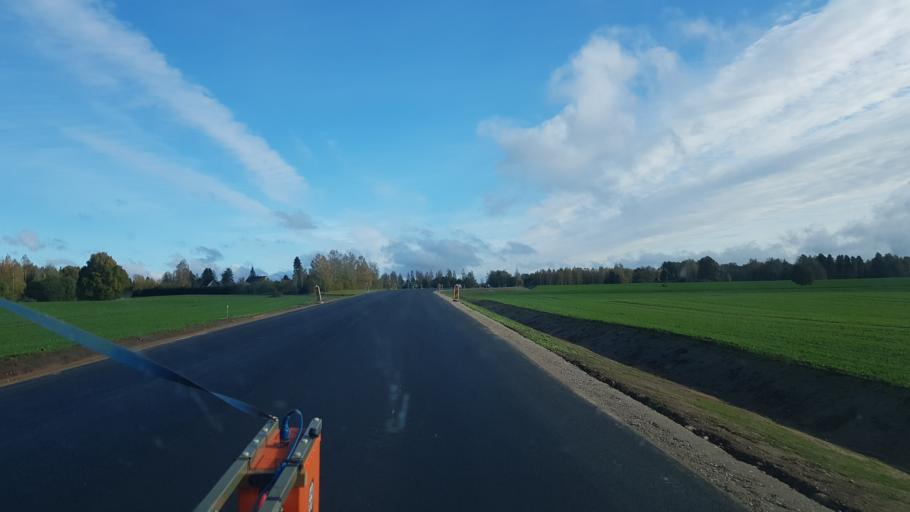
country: EE
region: Viljandimaa
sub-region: Suure-Jaani vald
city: Suure-Jaani
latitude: 58.3512
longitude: 25.3729
